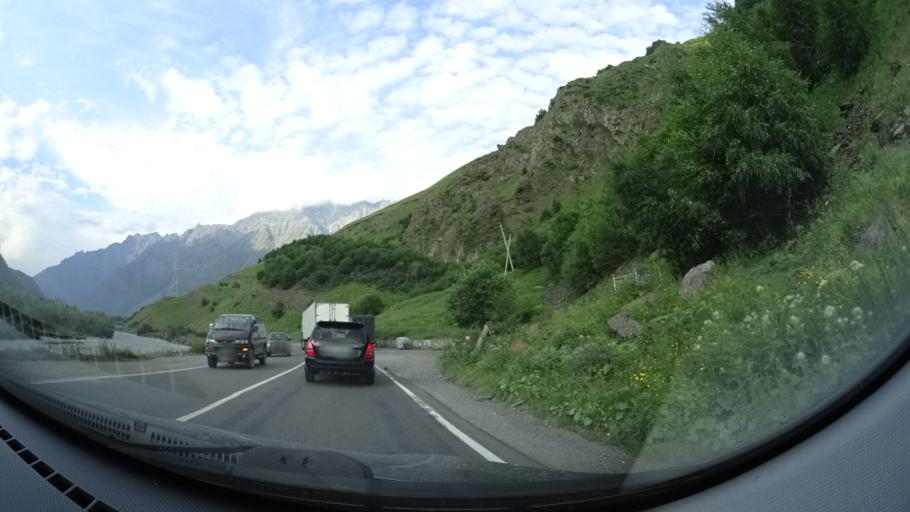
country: GE
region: Mtskheta-Mtianeti
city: Step'antsminda
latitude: 42.6383
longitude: 44.6338
